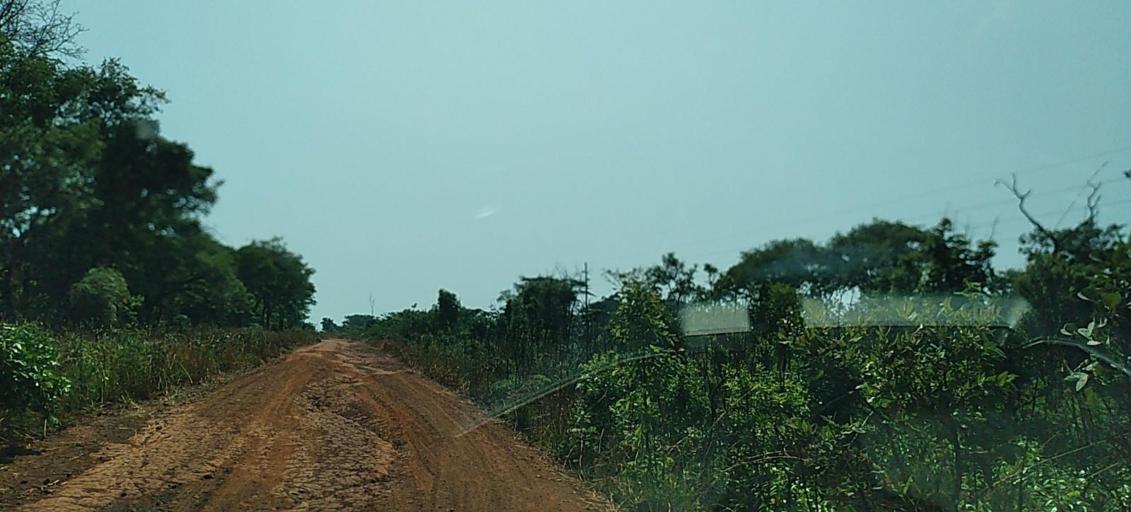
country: ZM
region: North-Western
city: Kansanshi
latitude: -12.0102
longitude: 26.5085
